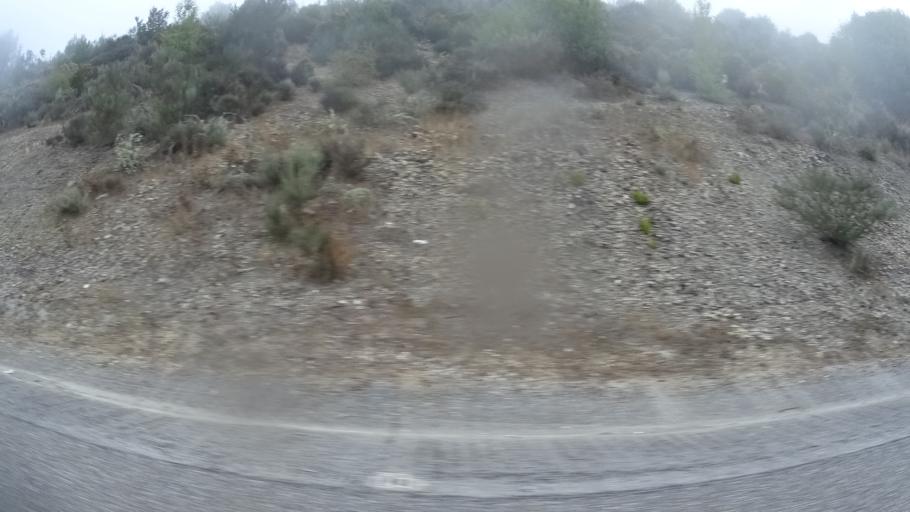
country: ES
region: Galicia
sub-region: Provincia de Lugo
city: Becerrea
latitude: 42.8222
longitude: -7.1127
